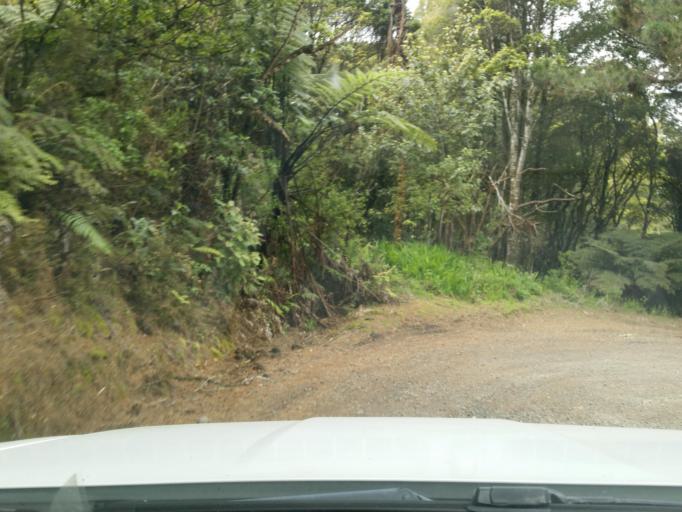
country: NZ
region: Northland
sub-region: Kaipara District
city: Dargaville
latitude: -35.7042
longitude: 173.6416
